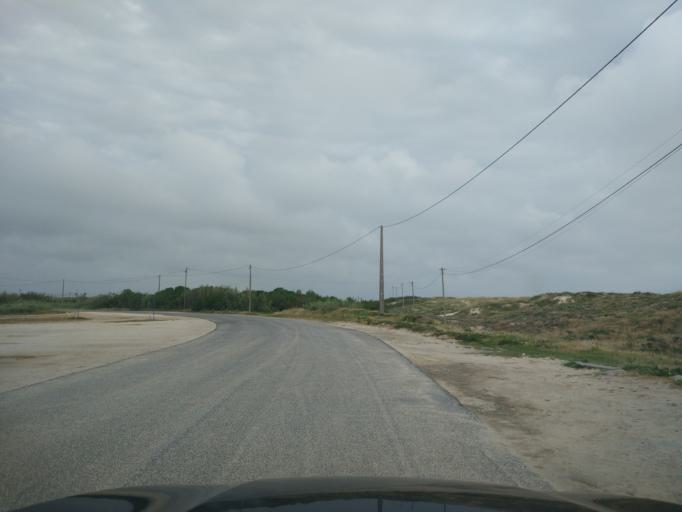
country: PT
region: Leiria
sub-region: Peniche
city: Peniche
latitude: 39.3502
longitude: -9.3652
